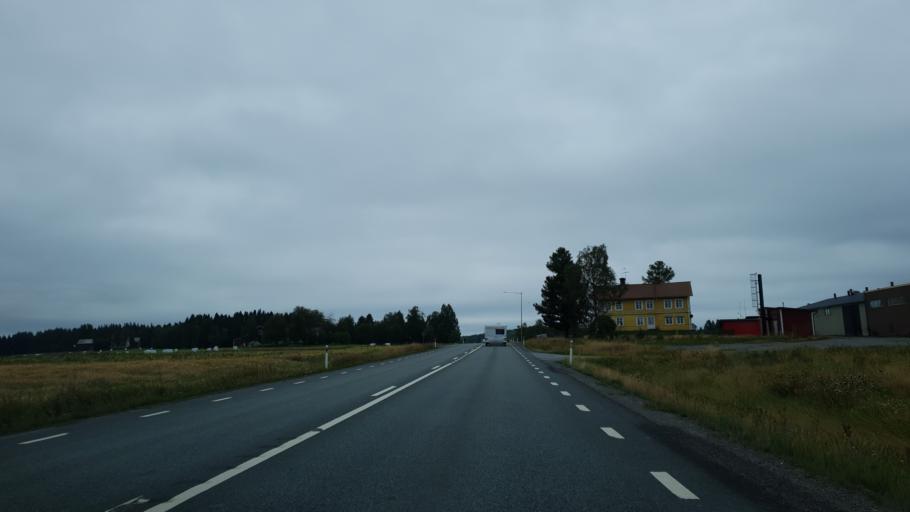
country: SE
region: Vaesterbotten
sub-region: Skelleftea Kommun
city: Burea
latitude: 64.3767
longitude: 21.3039
